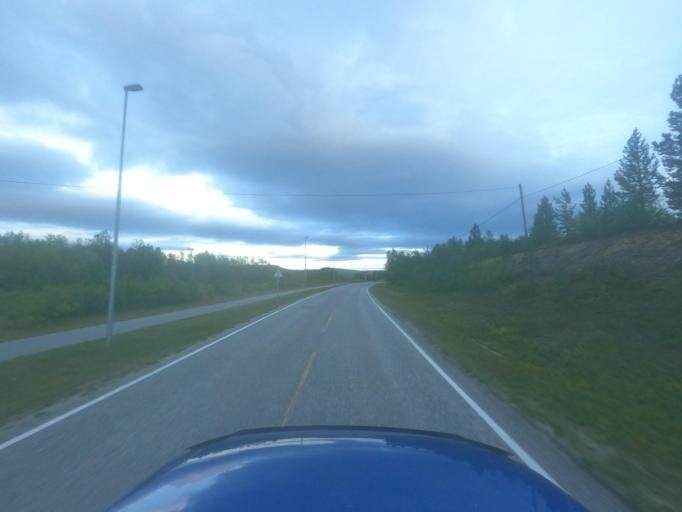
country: NO
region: Finnmark Fylke
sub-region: Porsanger
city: Lakselv
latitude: 69.9092
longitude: 24.9952
